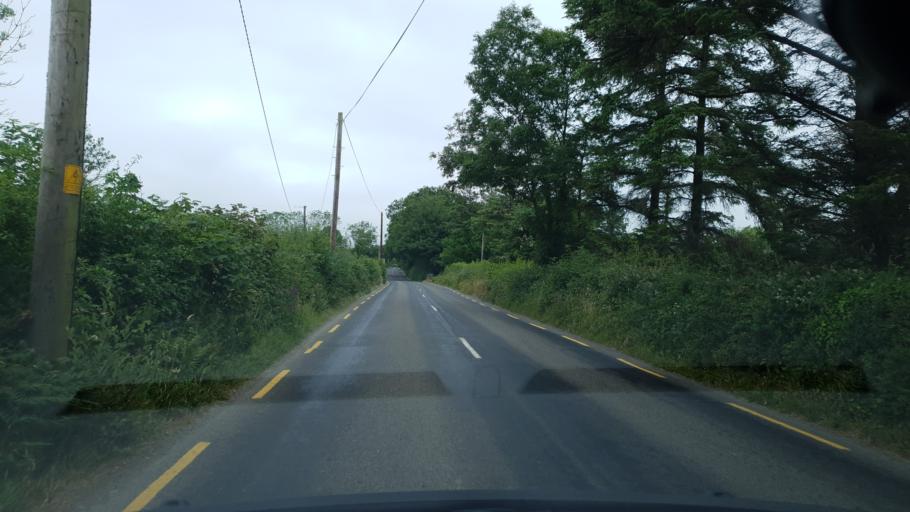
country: IE
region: Munster
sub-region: Ciarrai
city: Tralee
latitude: 52.1587
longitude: -9.6779
